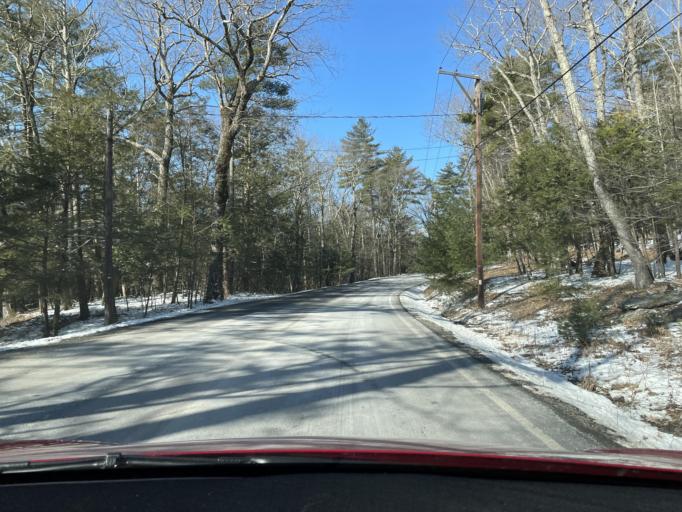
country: US
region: New York
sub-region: Ulster County
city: Woodstock
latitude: 42.0517
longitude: -74.1505
